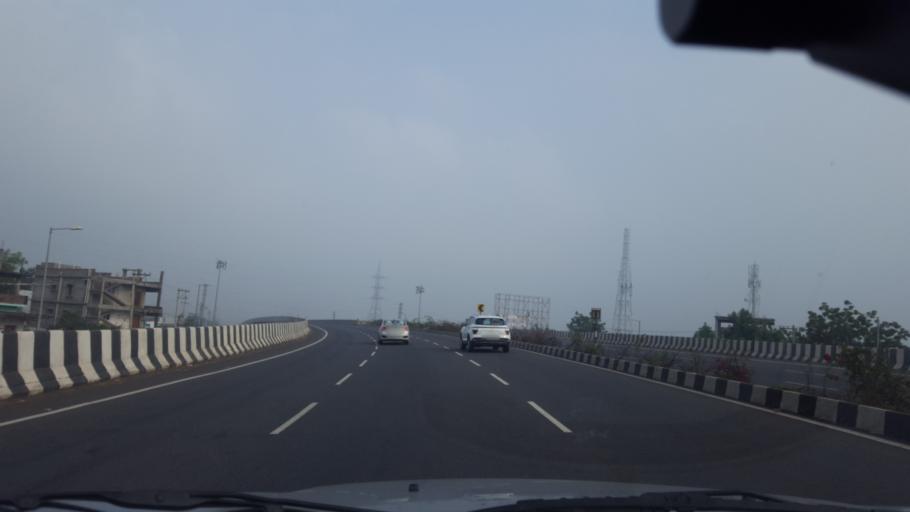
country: IN
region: Andhra Pradesh
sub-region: Prakasam
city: Ongole
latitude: 15.5509
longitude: 80.0560
